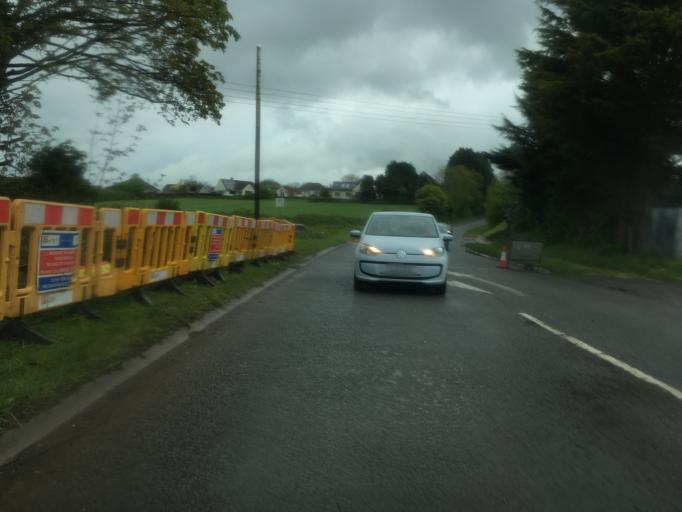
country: GB
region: England
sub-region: North Somerset
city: Sandford
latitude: 51.3322
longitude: -2.8432
